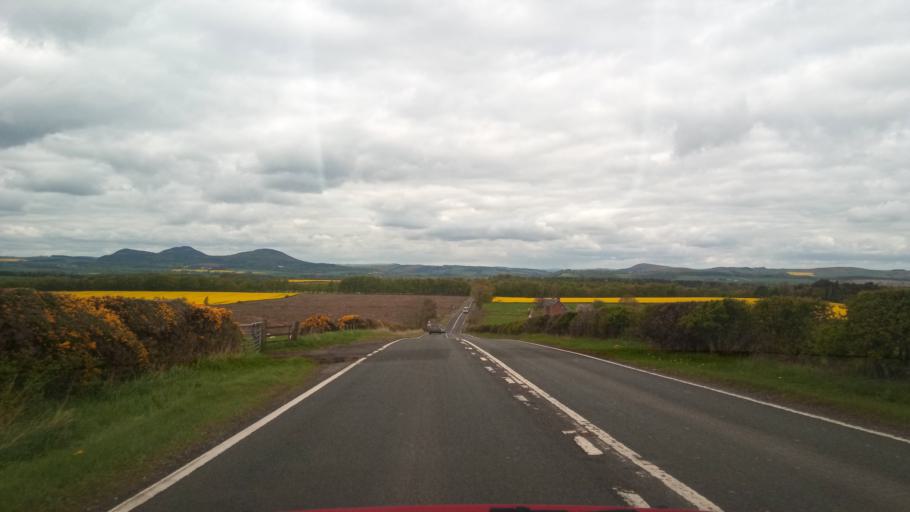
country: GB
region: Scotland
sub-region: The Scottish Borders
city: Saint Boswells
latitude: 55.5382
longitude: -2.6119
